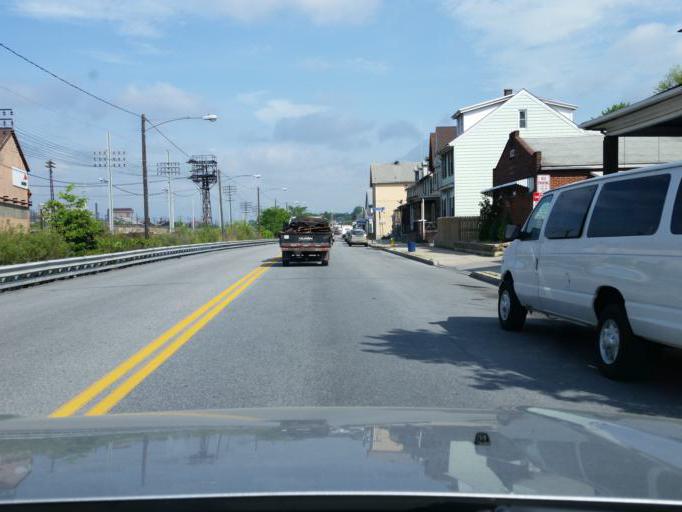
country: US
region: Pennsylvania
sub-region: Dauphin County
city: Enhaut
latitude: 40.2263
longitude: -76.8293
